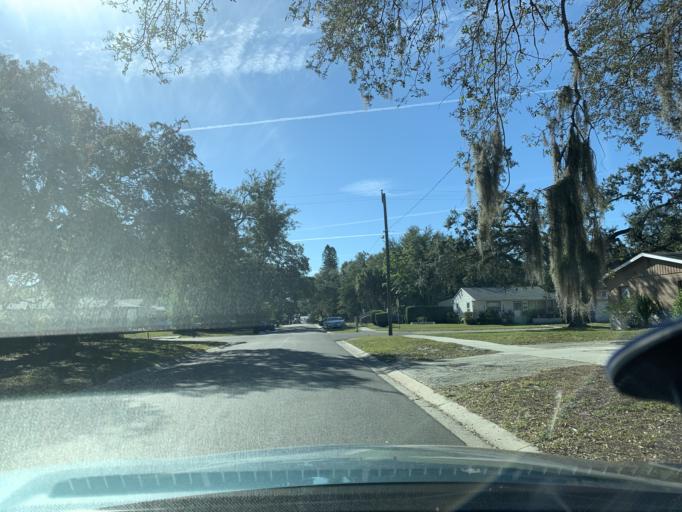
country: US
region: Florida
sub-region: Pinellas County
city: Gulfport
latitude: 27.7542
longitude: -82.6911
